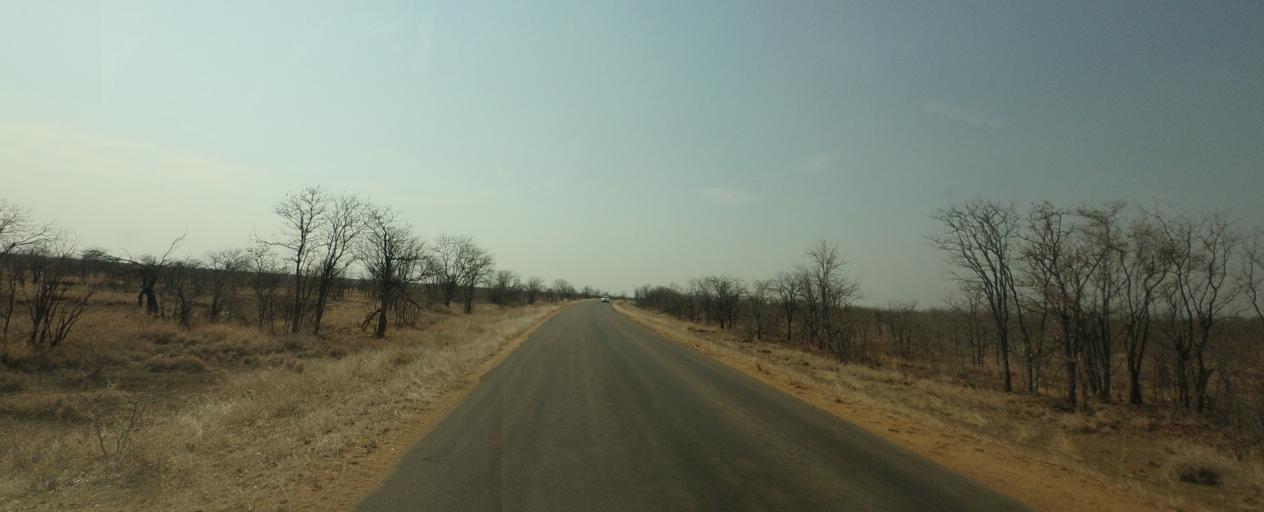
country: ZA
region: Limpopo
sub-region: Mopani District Municipality
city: Phalaborwa
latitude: -23.9414
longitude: 31.6128
